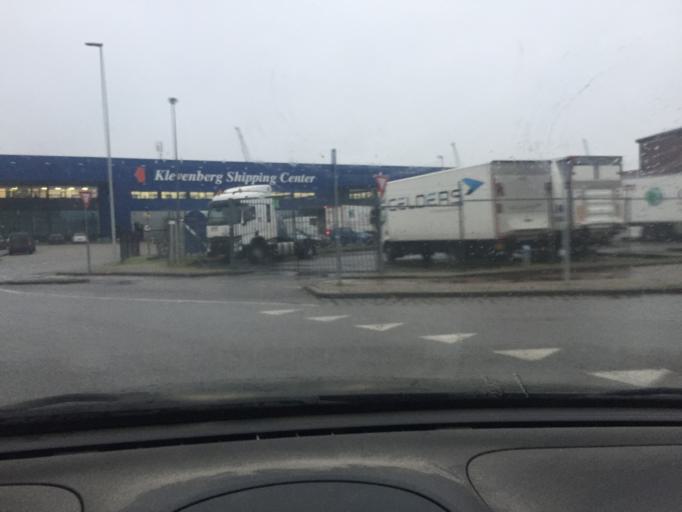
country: NL
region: South Holland
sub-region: Gemeente Albrandswaard
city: Rhoon
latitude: 51.8871
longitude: 4.4196
